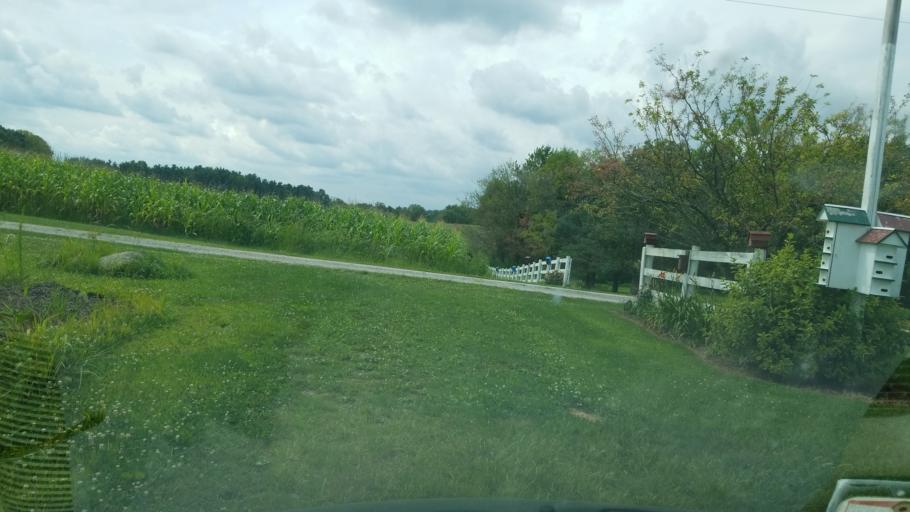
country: US
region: Ohio
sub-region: Morrow County
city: Mount Gilead
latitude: 40.5096
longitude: -82.7220
